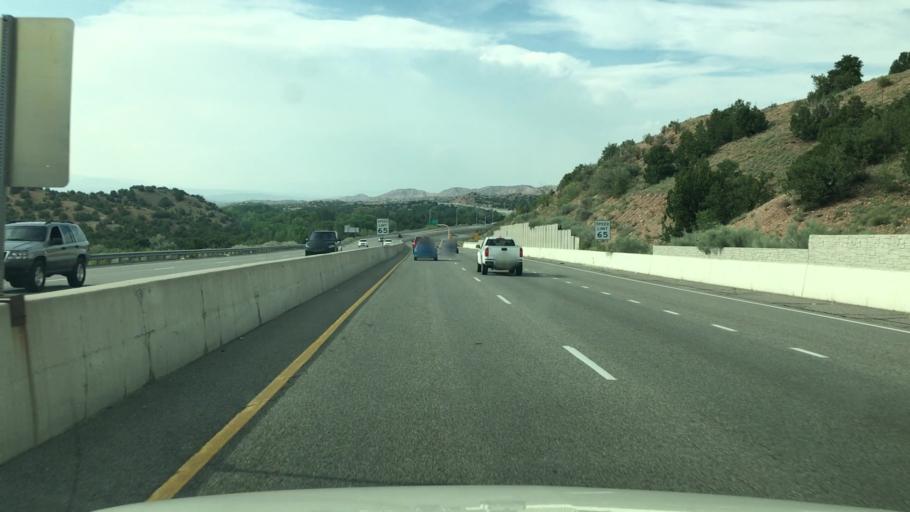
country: US
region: New Mexico
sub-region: Santa Fe County
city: Santa Fe
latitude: 35.7760
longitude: -105.9461
